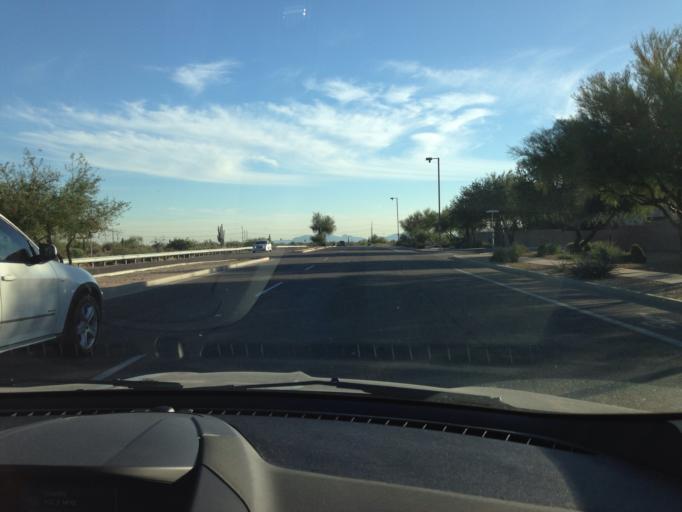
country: US
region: Arizona
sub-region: Maricopa County
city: Cave Creek
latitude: 33.7218
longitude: -111.9773
